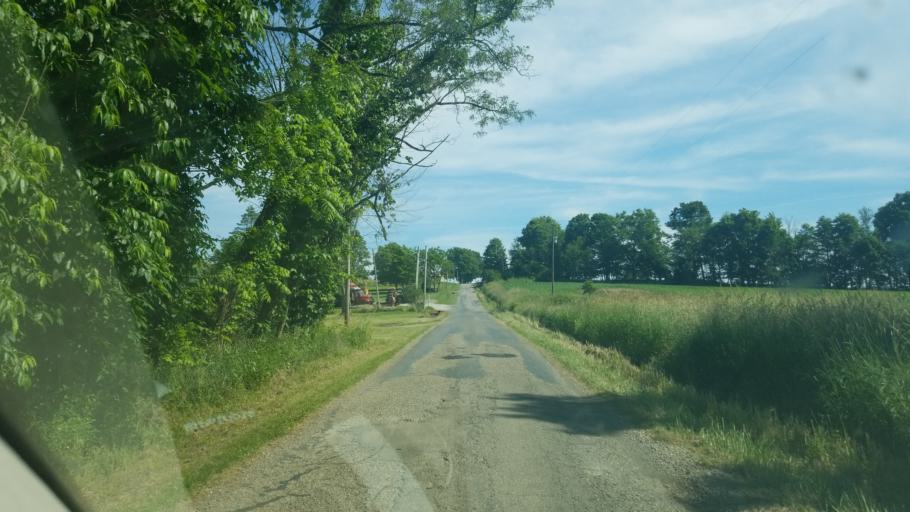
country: US
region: Ohio
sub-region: Holmes County
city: Millersburg
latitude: 40.4816
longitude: -81.9638
